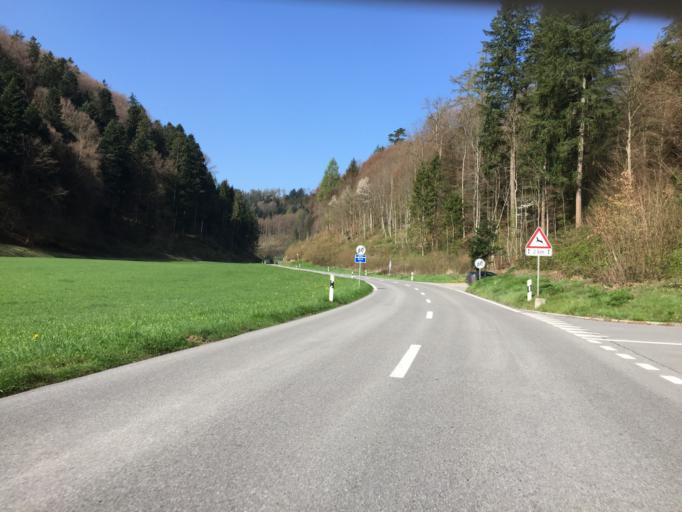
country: CH
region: Bern
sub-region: Bern-Mittelland District
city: Bariswil
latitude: 46.9989
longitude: 7.5307
